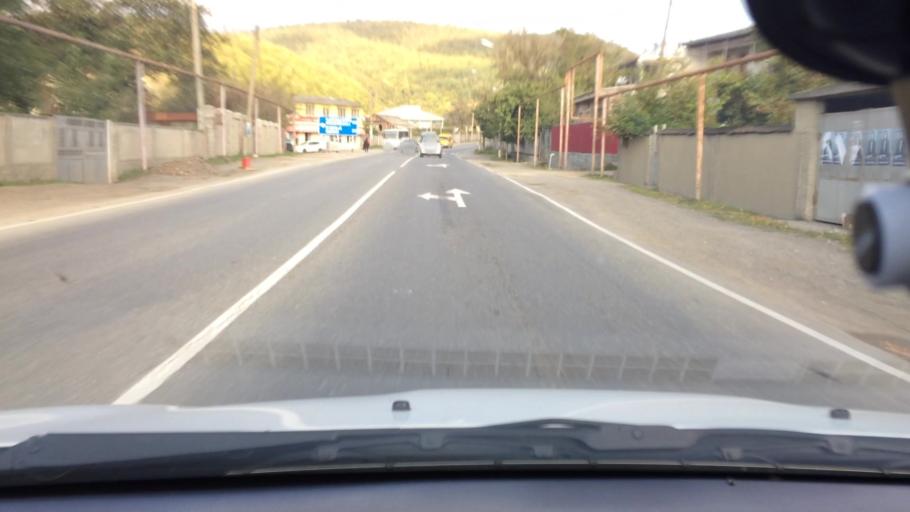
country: GE
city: Surami
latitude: 42.0303
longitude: 43.5266
